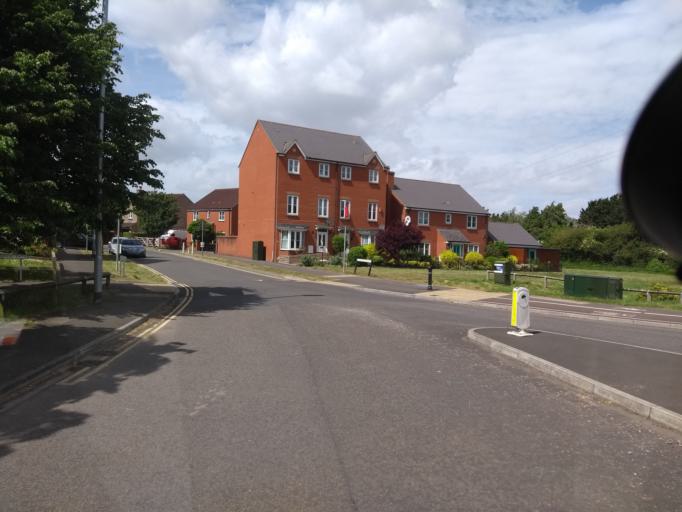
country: GB
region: England
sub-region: Somerset
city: Bridgwater
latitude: 51.1122
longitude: -2.9955
